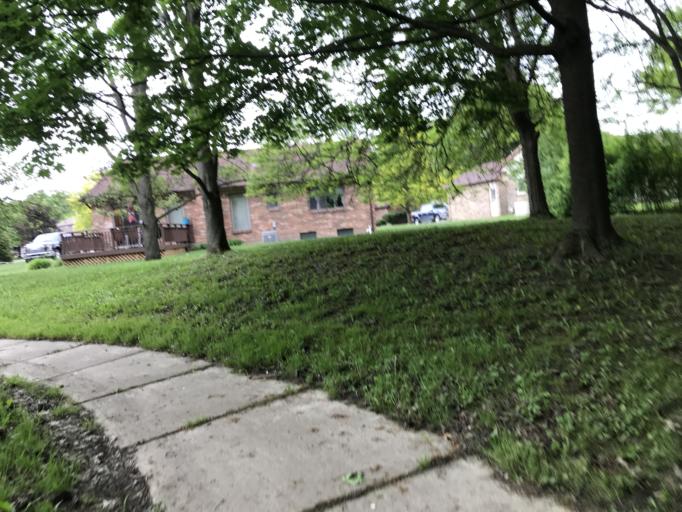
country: US
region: Michigan
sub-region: Oakland County
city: Farmington
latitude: 42.4662
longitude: -83.3300
